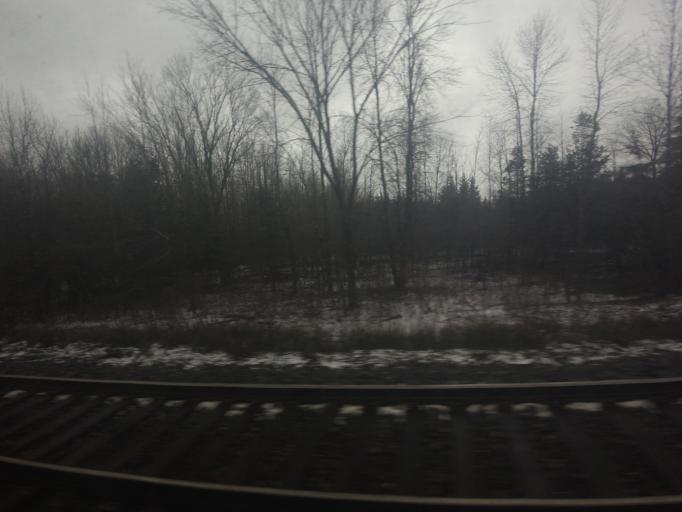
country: CA
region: Ontario
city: Belleville
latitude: 44.2032
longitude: -77.2522
